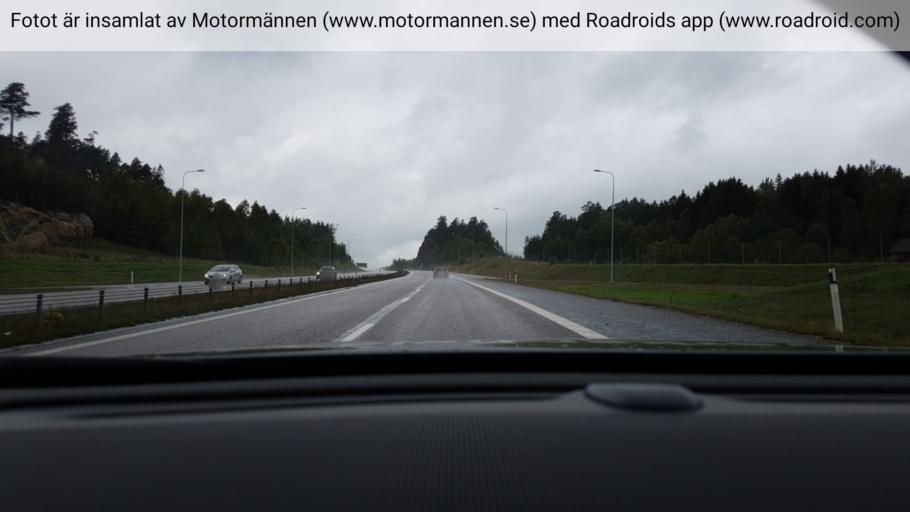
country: SE
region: Vaestra Goetaland
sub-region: Uddevalla Kommun
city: Uddevalla
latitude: 58.3575
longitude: 11.8089
